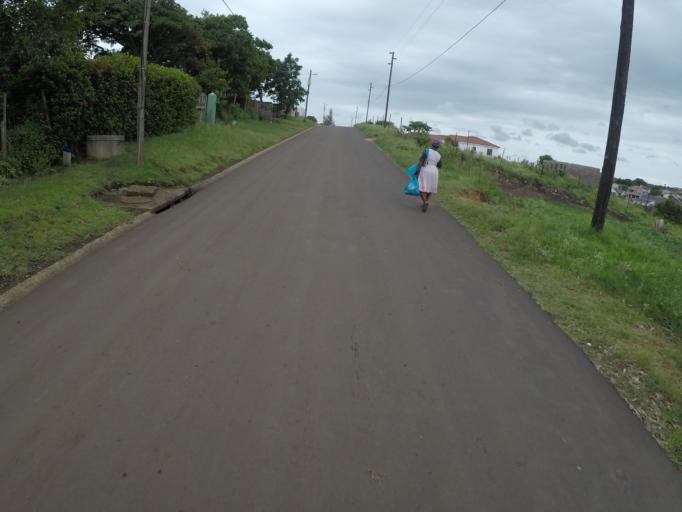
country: ZA
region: KwaZulu-Natal
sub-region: uThungulu District Municipality
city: Empangeni
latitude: -28.7745
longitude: 31.8537
